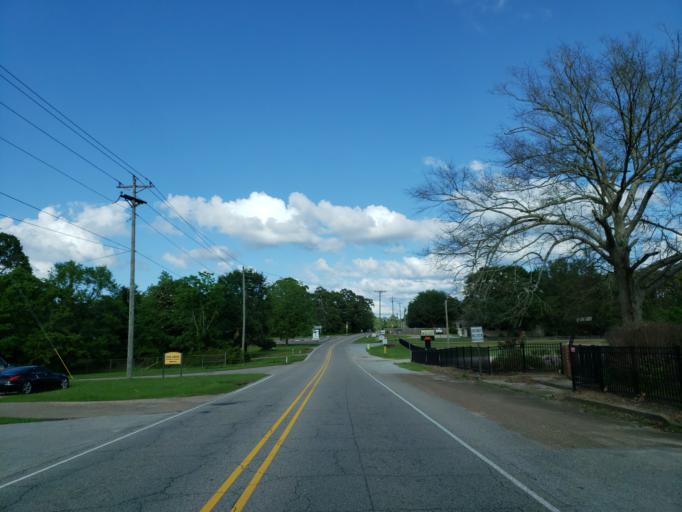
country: US
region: Mississippi
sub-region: Lamar County
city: West Hattiesburg
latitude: 31.2860
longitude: -89.4193
